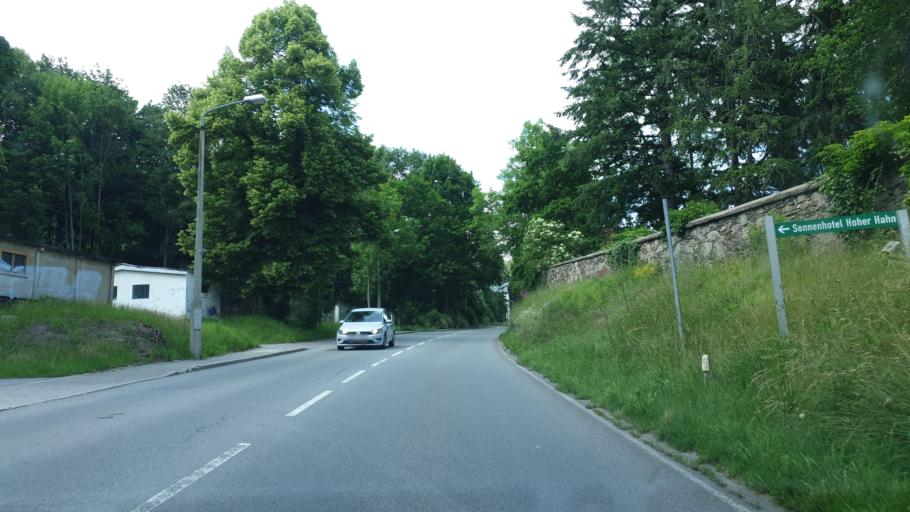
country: DE
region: Saxony
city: Schwarzenberg
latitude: 50.5359
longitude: 12.7798
